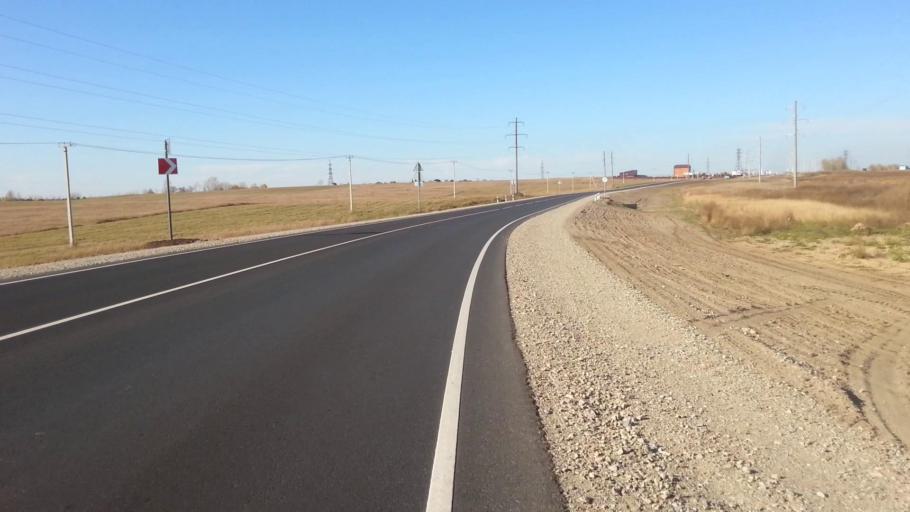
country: RU
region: Altai Krai
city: Sannikovo
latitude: 53.3295
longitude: 83.9389
